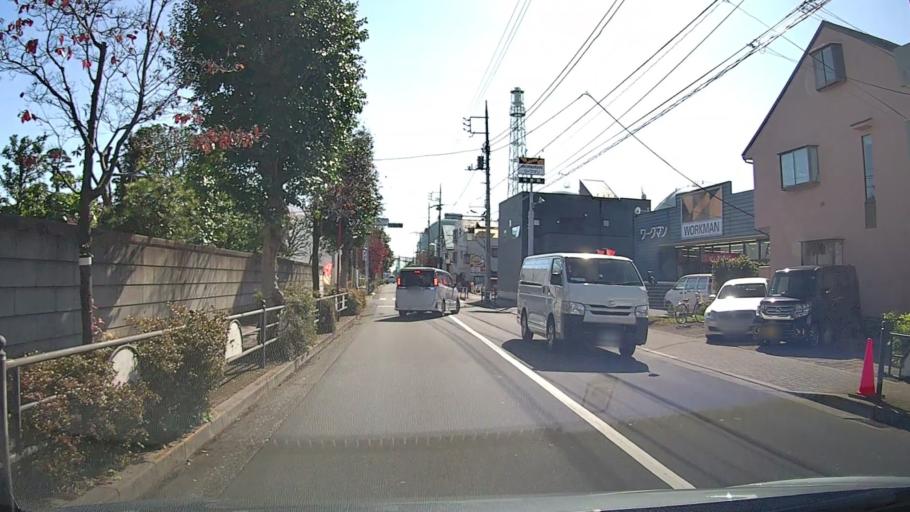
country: JP
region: Saitama
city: Wako
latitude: 35.7499
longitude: 139.6257
